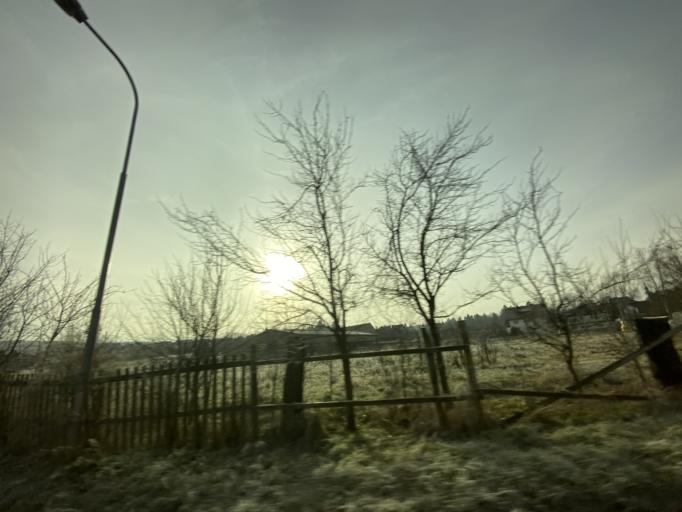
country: DE
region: Hesse
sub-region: Regierungsbezirk Giessen
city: Ebsdorfergrund
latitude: 50.7620
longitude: 8.8844
